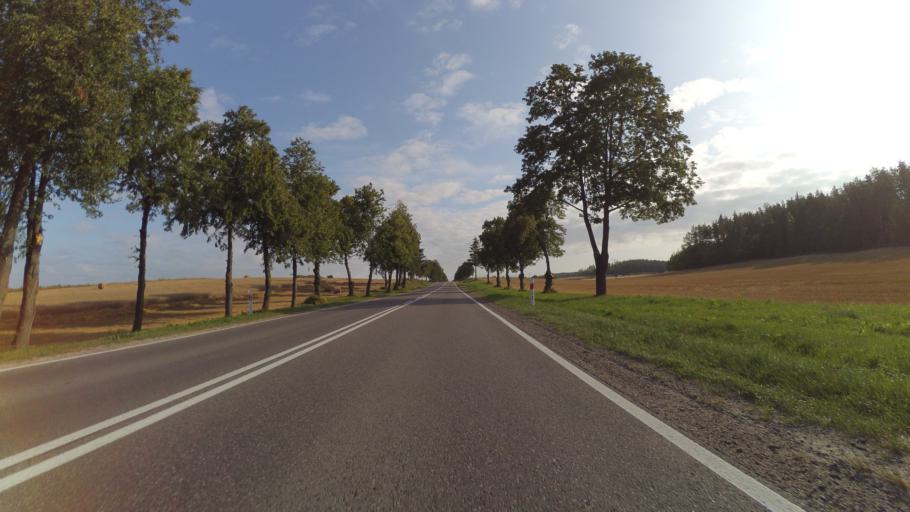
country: PL
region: Podlasie
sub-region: Powiat sokolski
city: Sokolka
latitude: 53.3549
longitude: 23.4144
